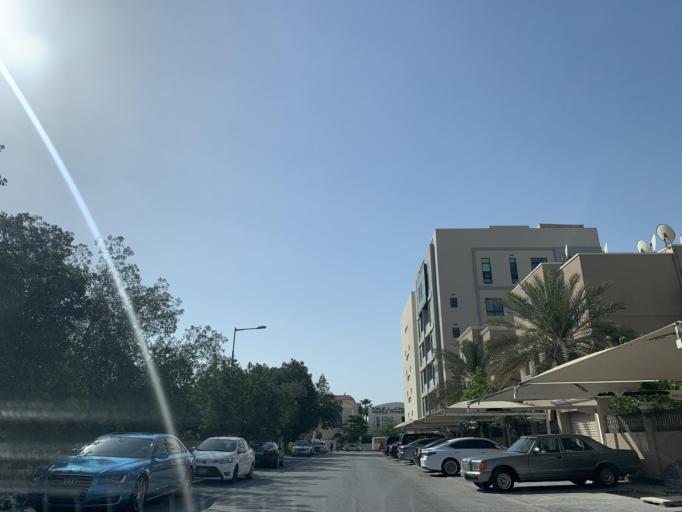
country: BH
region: Manama
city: Manama
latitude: 26.2105
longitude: 50.5873
